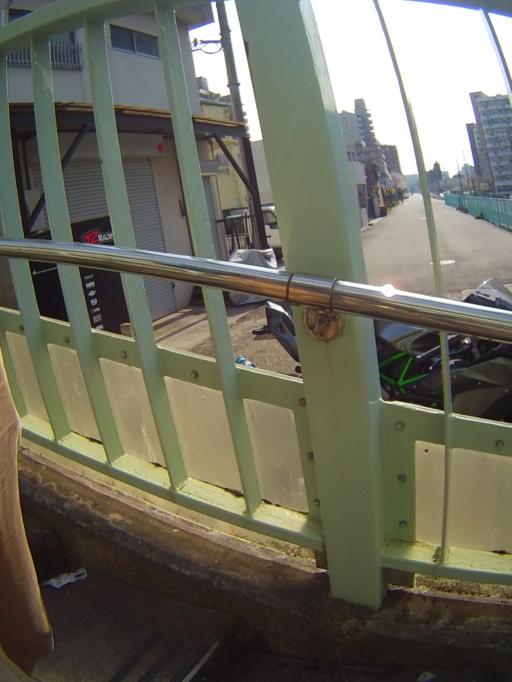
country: JP
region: Hyogo
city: Amagasaki
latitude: 34.6862
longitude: 135.4519
